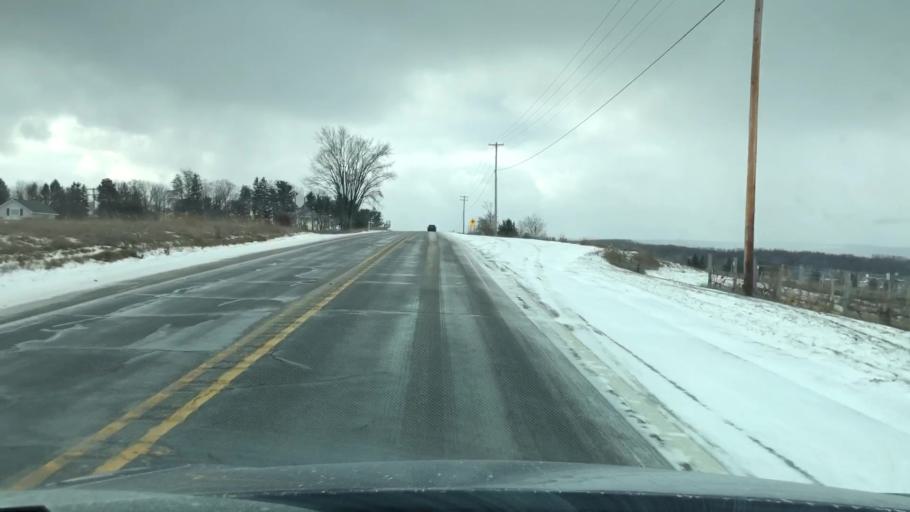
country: US
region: Michigan
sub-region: Antrim County
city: Elk Rapids
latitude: 44.8641
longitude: -85.5183
